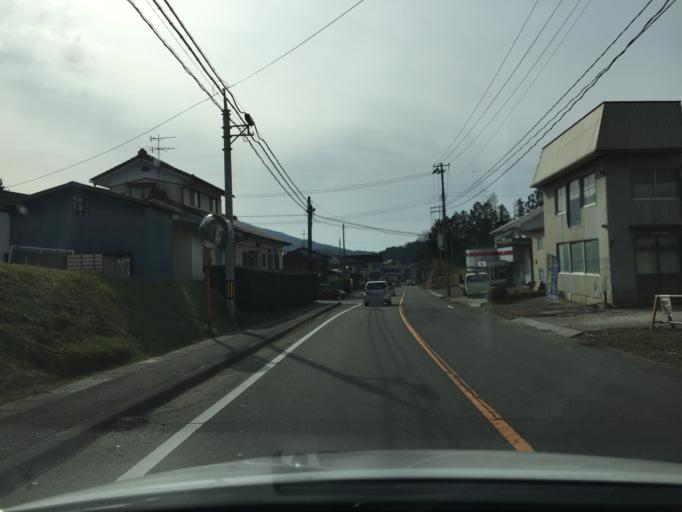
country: JP
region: Fukushima
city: Funehikimachi-funehiki
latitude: 37.4508
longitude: 140.5742
